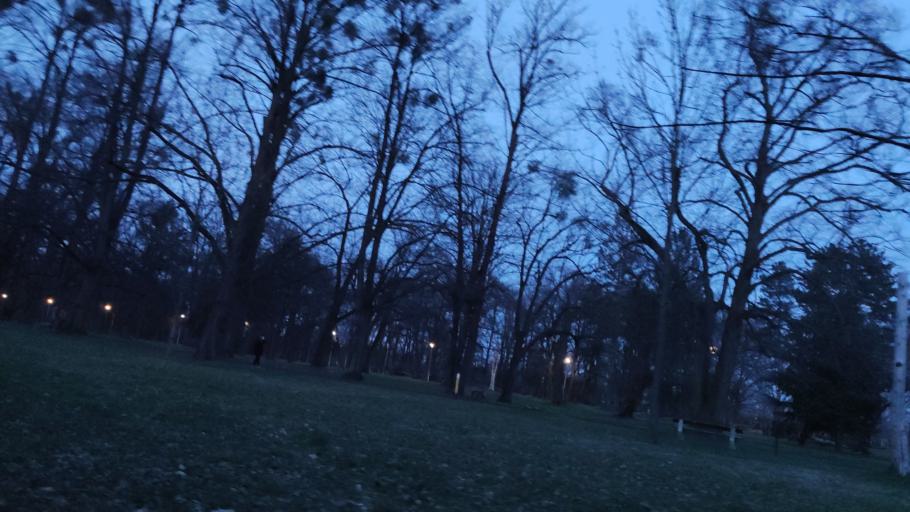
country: PL
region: Lower Silesian Voivodeship
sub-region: Powiat wroclawski
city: Wroclaw
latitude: 51.0772
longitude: 17.0243
